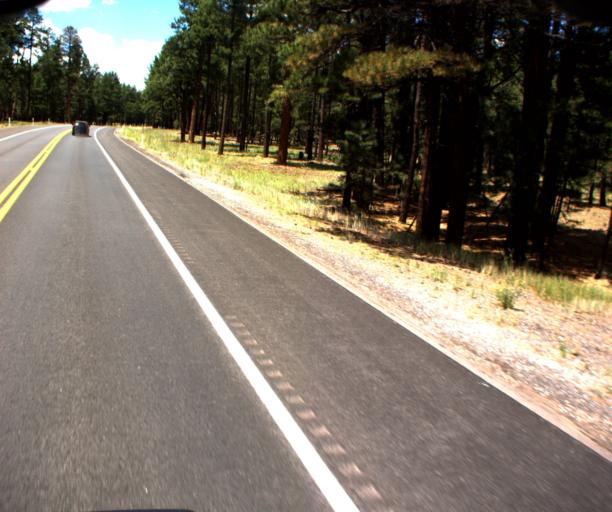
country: US
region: Arizona
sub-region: Coconino County
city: Flagstaff
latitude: 35.2503
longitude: -111.6946
